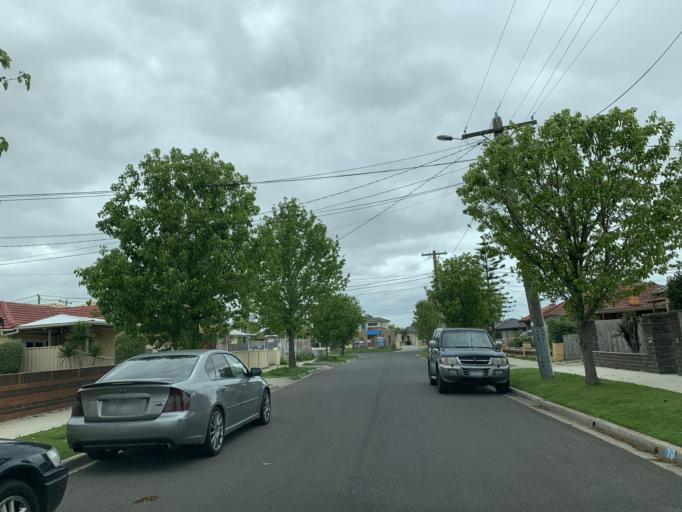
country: AU
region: Victoria
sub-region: Brimbank
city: St Albans
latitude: -37.7388
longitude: 144.8111
